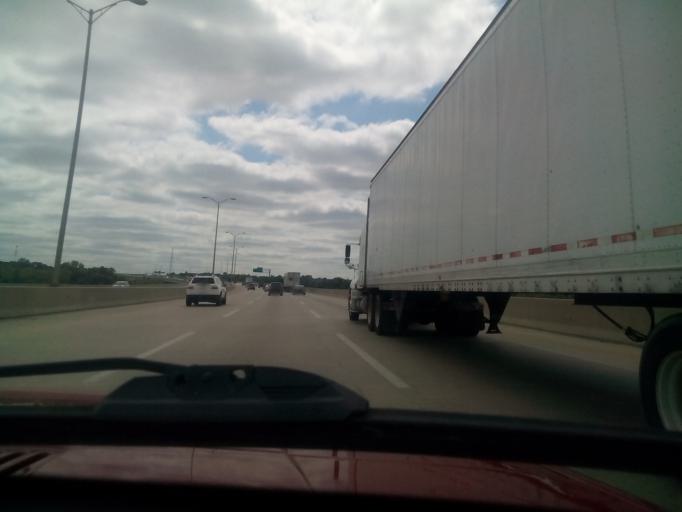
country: US
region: Illinois
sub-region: Cook County
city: Lemont
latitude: 41.6712
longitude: -88.0289
